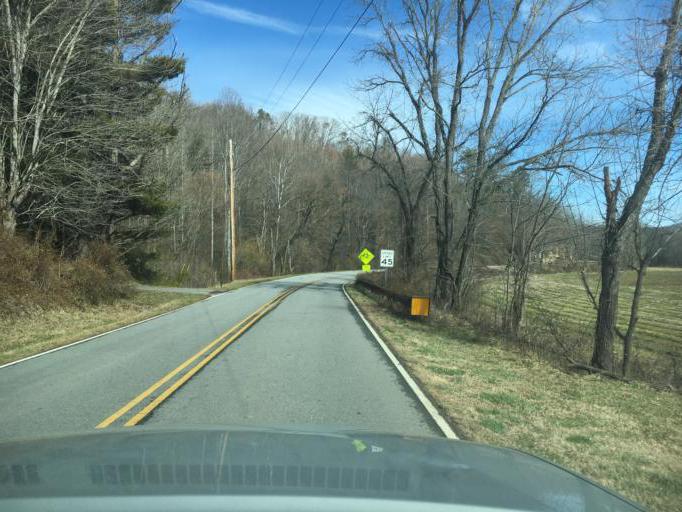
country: US
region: North Carolina
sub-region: Haywood County
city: West Canton
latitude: 35.5009
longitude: -82.8736
